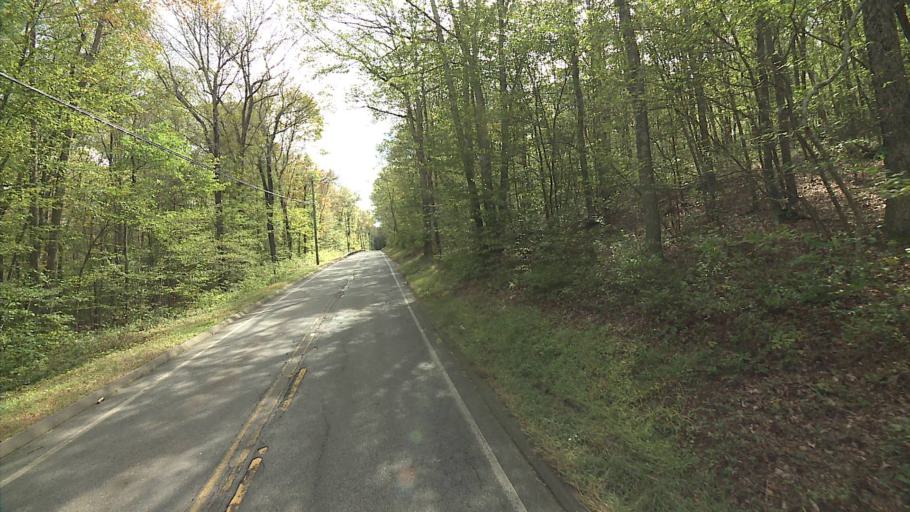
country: US
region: Connecticut
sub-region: Middlesex County
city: Durham
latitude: 41.4206
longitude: -72.6222
